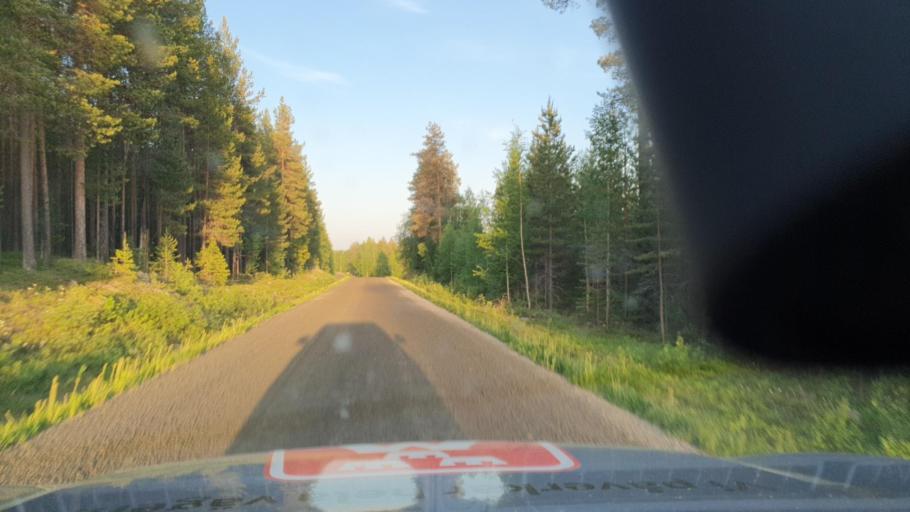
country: SE
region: Norrbotten
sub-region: Bodens Kommun
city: Boden
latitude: 66.0584
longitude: 21.7373
